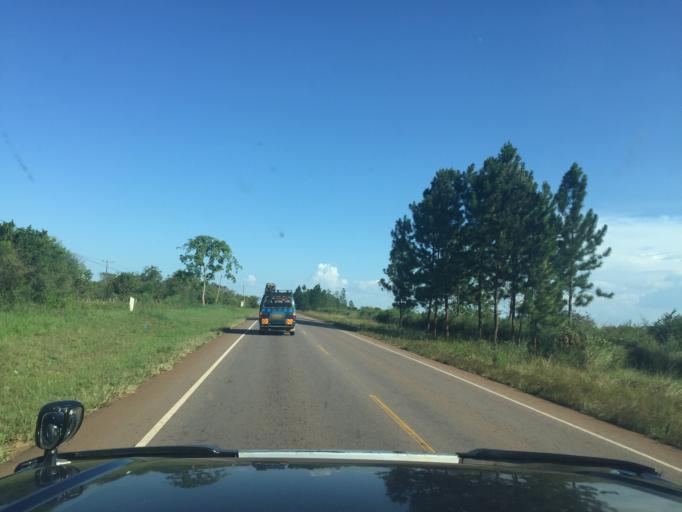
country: UG
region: Central Region
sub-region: Nakasongola District
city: Nakasongola
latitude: 1.3861
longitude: 32.3307
